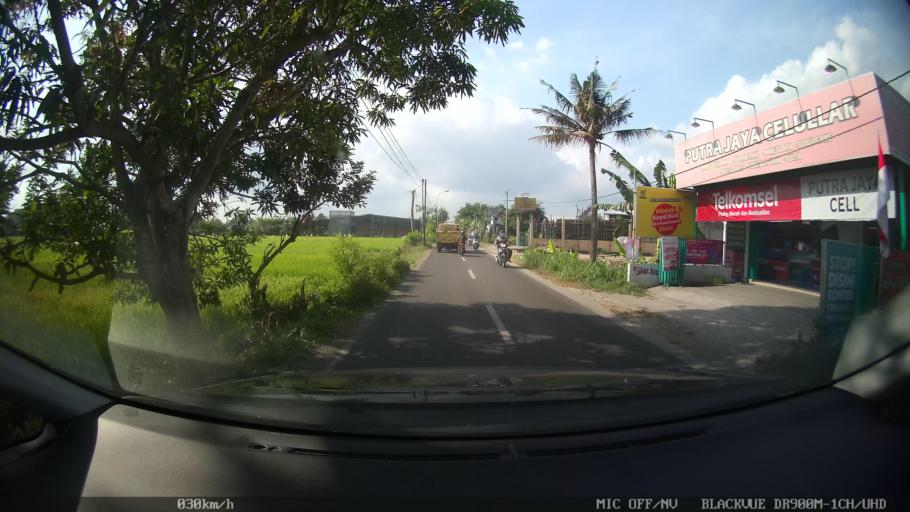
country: ID
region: Daerah Istimewa Yogyakarta
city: Kasihan
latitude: -7.8453
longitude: 110.3431
